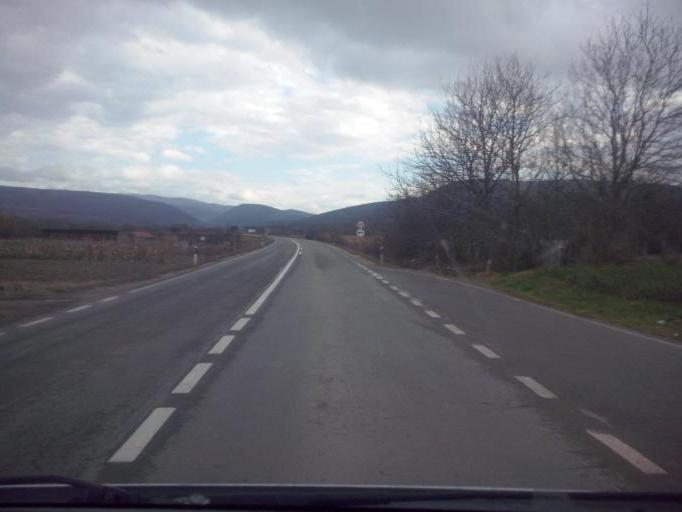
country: RS
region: Central Serbia
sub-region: Pomoravski Okrug
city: Paracin
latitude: 43.8552
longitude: 21.5596
